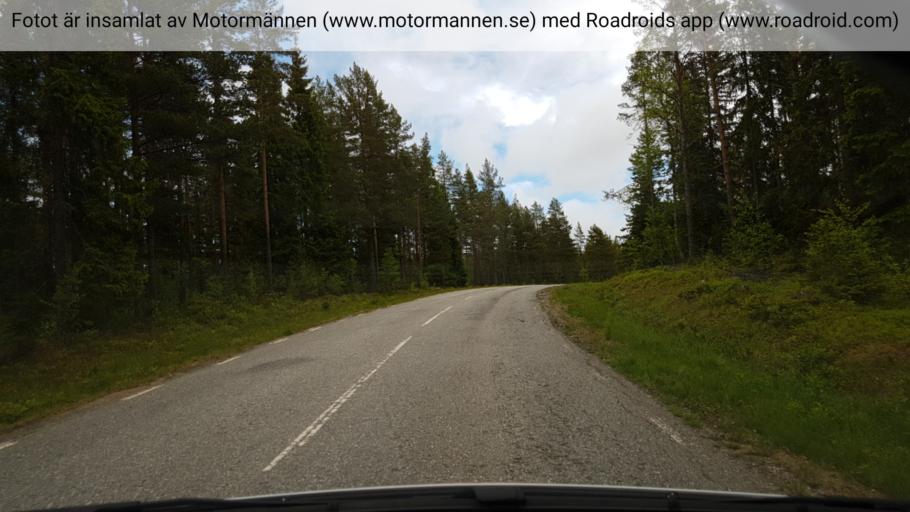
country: SE
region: Vaesterbotten
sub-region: Umea Kommun
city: Hoernefors
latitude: 63.5662
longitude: 19.7996
